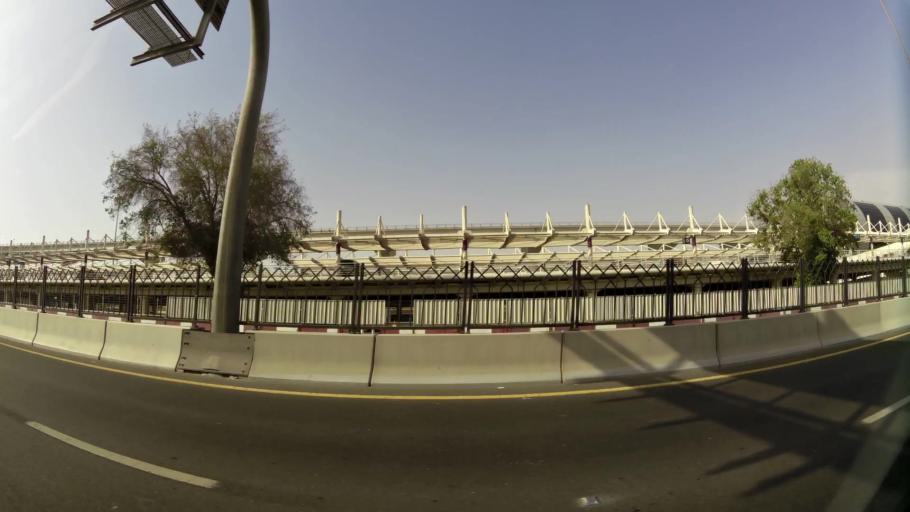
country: AE
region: Ash Shariqah
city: Sharjah
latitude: 25.2483
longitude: 55.3509
